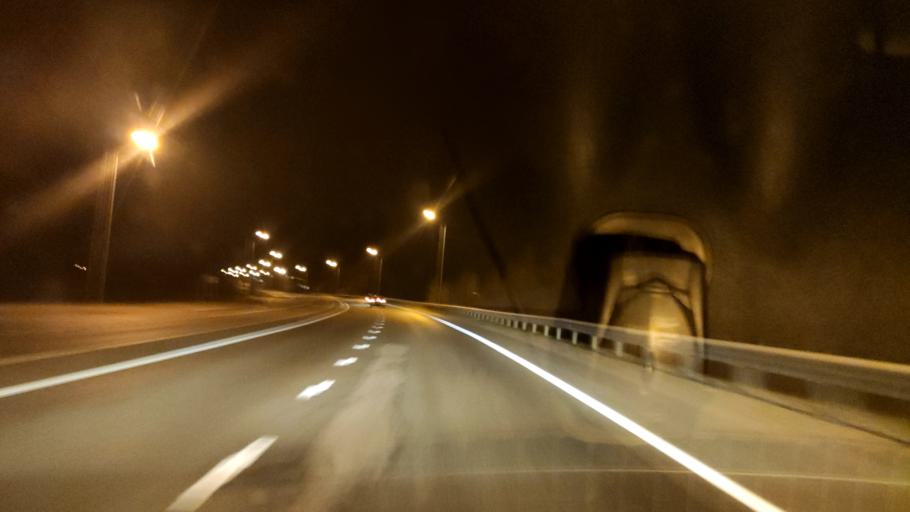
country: RU
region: Belgorod
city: Staryy Oskol
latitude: 51.3469
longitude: 37.8227
